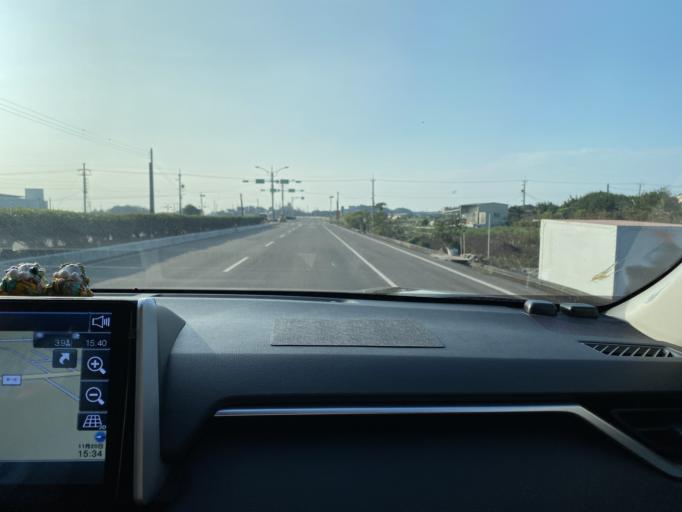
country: TW
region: Taiwan
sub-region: Changhua
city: Chang-hua
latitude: 23.9624
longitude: 120.3757
